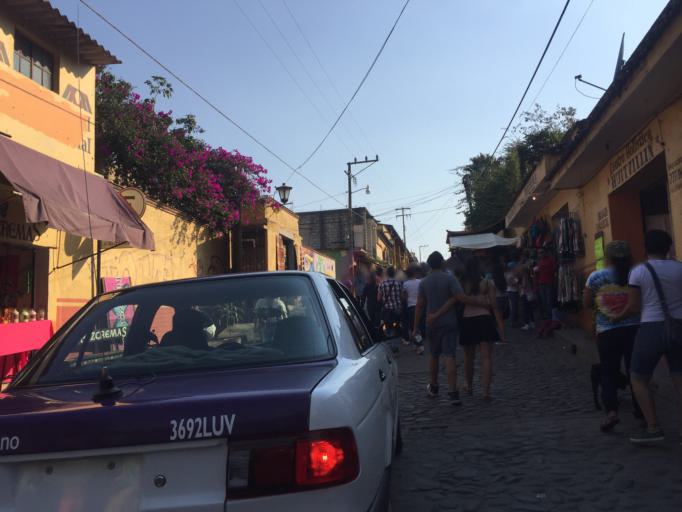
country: MX
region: Morelos
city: Tepoztlan
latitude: 18.9903
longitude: -99.1005
